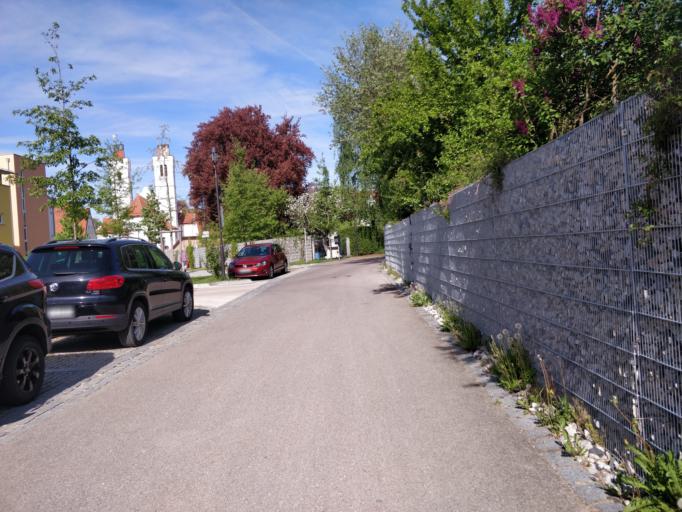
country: DE
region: Bavaria
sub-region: Swabia
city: Wertingen
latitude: 48.5617
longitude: 10.6853
